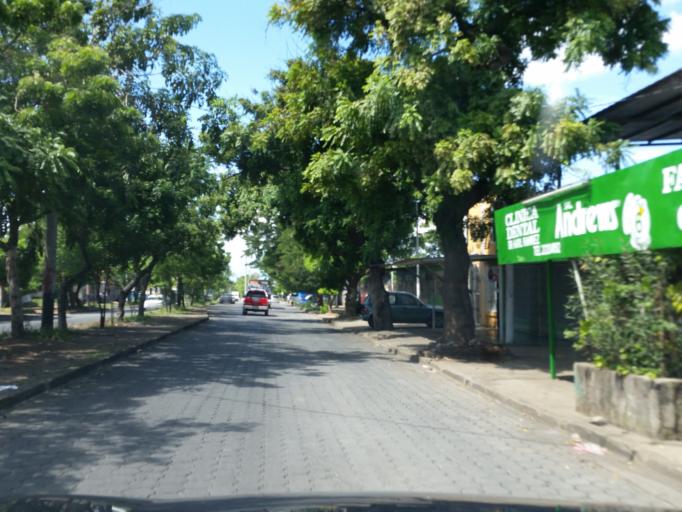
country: NI
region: Managua
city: Managua
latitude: 12.1329
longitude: -86.2171
